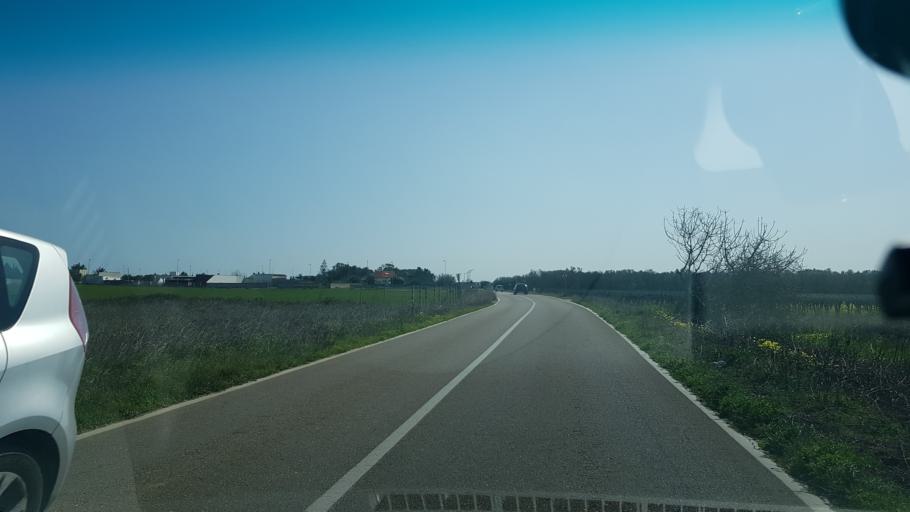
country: IT
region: Apulia
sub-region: Provincia di Brindisi
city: Torchiarolo
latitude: 40.5107
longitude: 18.0890
